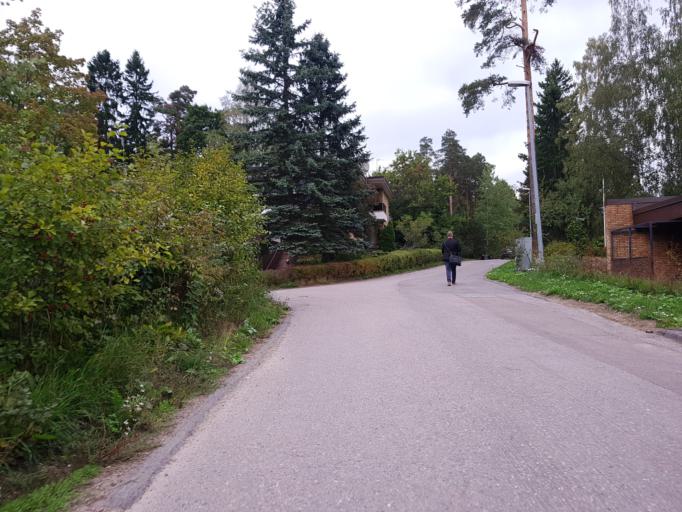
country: FI
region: Uusimaa
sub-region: Helsinki
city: Helsinki
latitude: 60.2288
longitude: 24.9796
